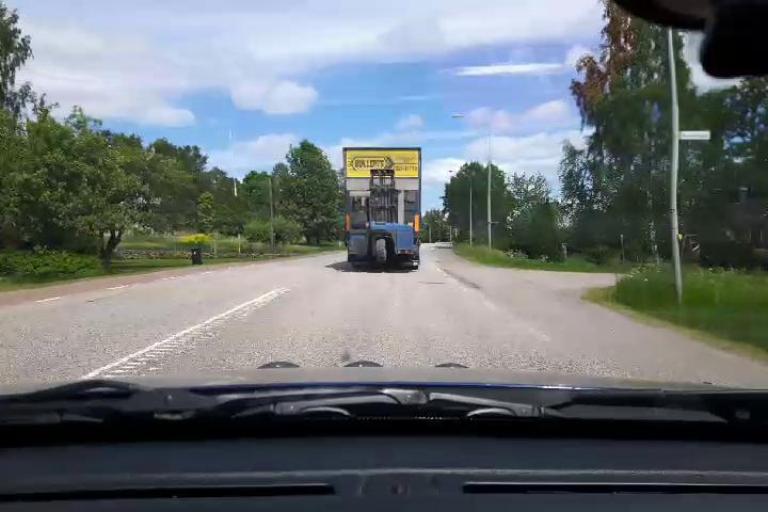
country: SE
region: Uppsala
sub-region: Osthammars Kommun
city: Bjorklinge
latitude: 60.0876
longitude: 17.5521
